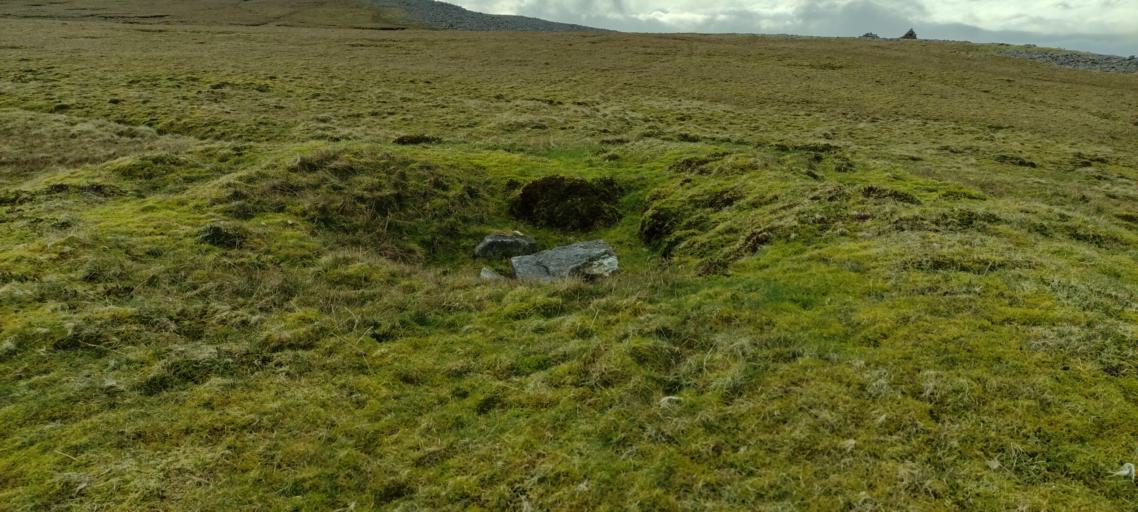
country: GB
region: England
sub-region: Cumbria
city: Appleby-in-Westmorland
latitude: 54.7387
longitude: -2.5507
